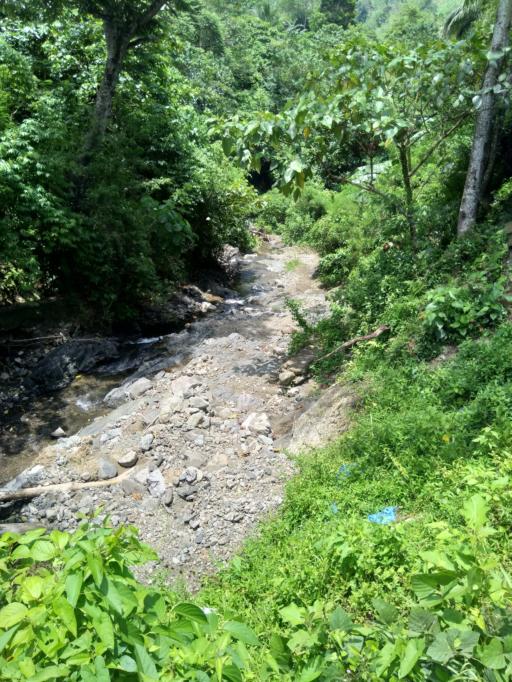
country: PH
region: Davao
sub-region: Province of Davao del Norte
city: Santo Nino
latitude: 7.6178
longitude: 125.5198
